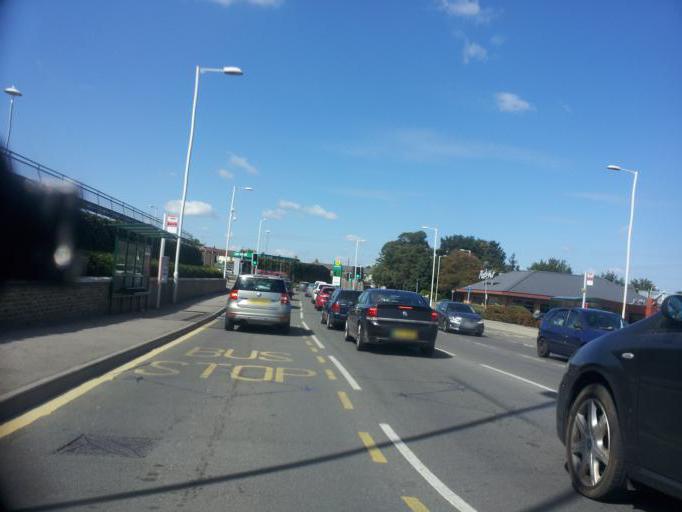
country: GB
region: England
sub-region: Kent
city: Sittingbourne
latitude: 51.3439
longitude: 0.7330
